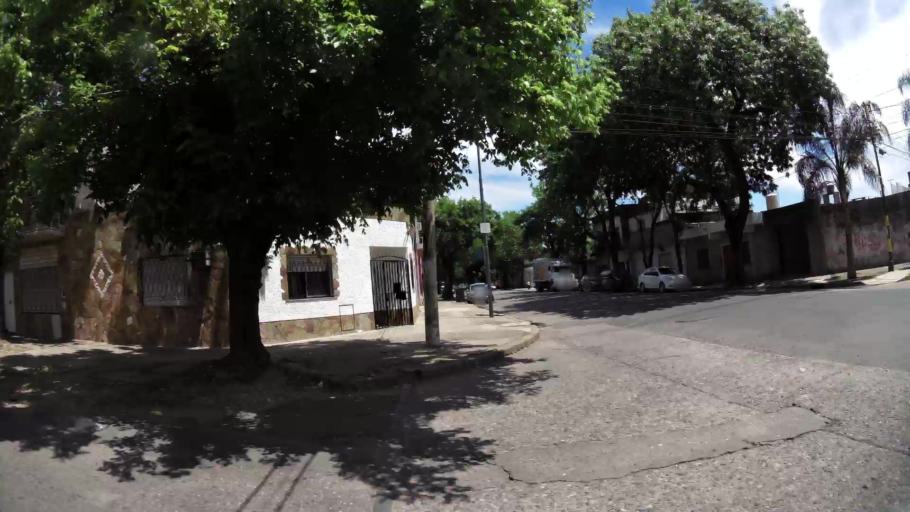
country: AR
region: Santa Fe
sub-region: Departamento de Rosario
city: Rosario
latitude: -32.9796
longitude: -60.6305
